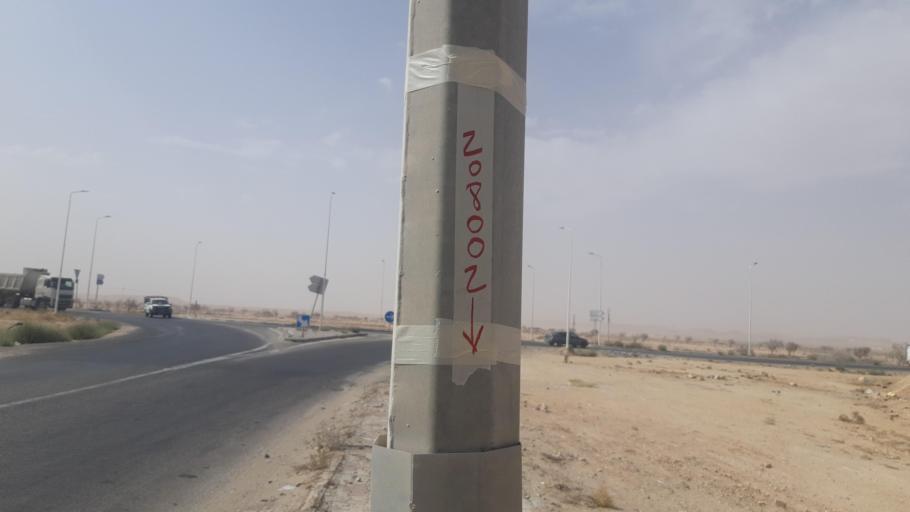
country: TN
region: Qabis
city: Gabes
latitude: 33.8757
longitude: 9.9764
